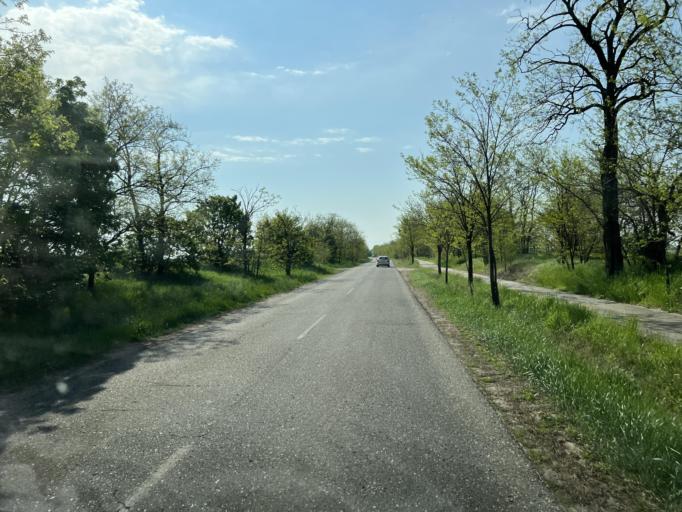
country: HU
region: Pest
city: Jaszkarajeno
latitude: 47.0862
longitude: 20.0346
